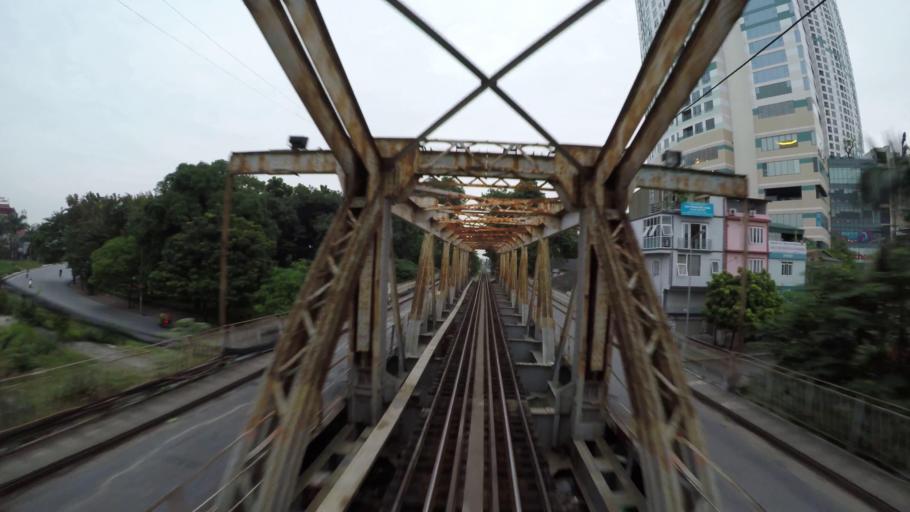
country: VN
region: Ha Noi
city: Hoan Kiem
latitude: 21.0505
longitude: 105.8913
